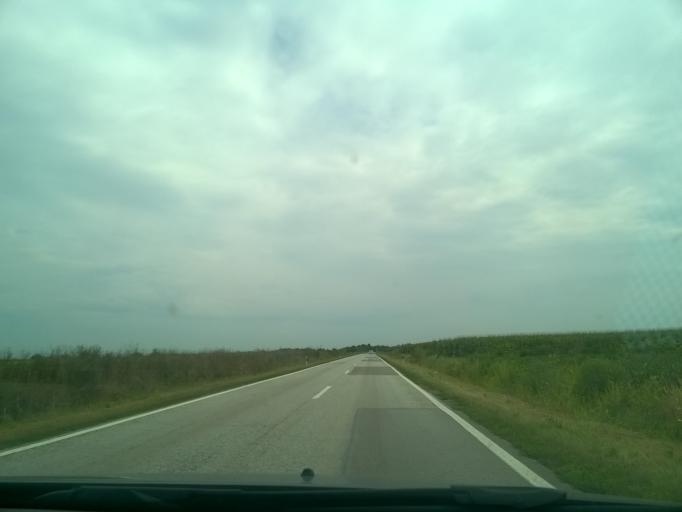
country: RS
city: Sutjeska
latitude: 45.3816
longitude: 20.7184
